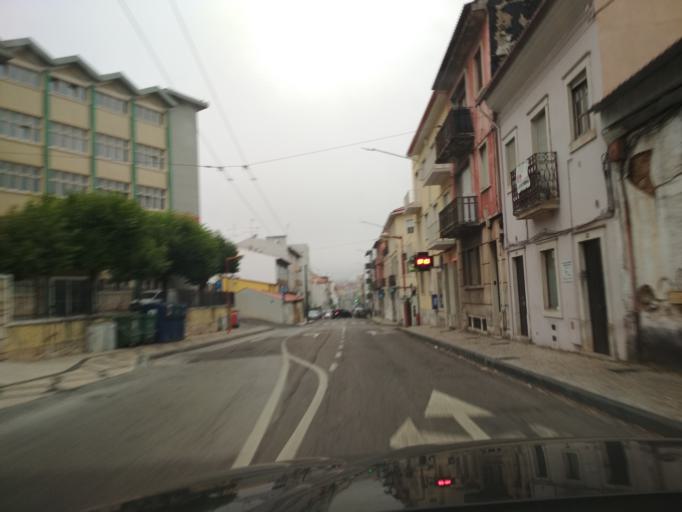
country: PT
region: Coimbra
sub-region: Coimbra
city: Coimbra
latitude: 40.1998
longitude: -8.4204
